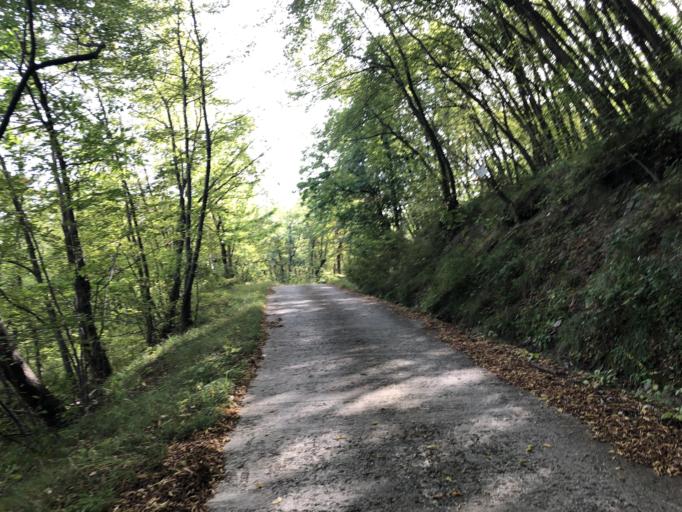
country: IT
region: Emilia-Romagna
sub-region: Forli-Cesena
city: Portico e San Benedetto
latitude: 44.0154
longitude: 11.7855
